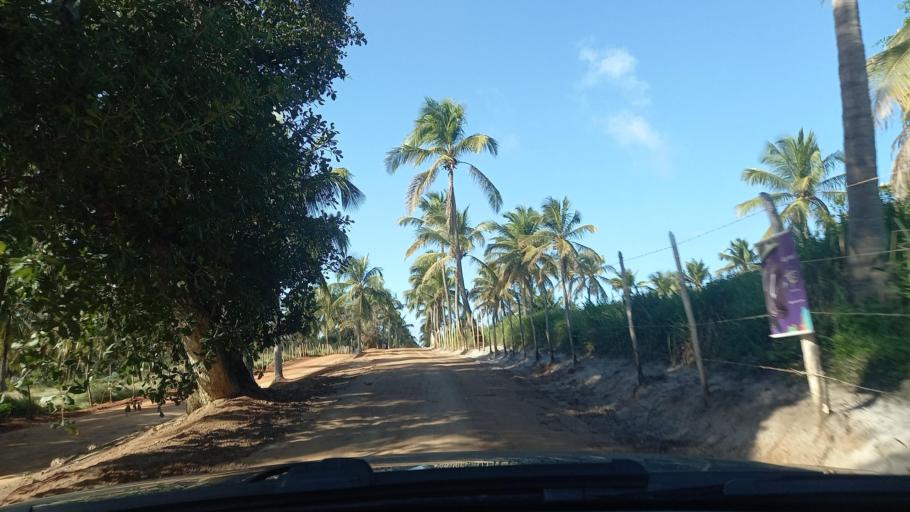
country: BR
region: Alagoas
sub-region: Marechal Deodoro
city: Marechal Deodoro
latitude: -9.8625
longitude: -35.9122
